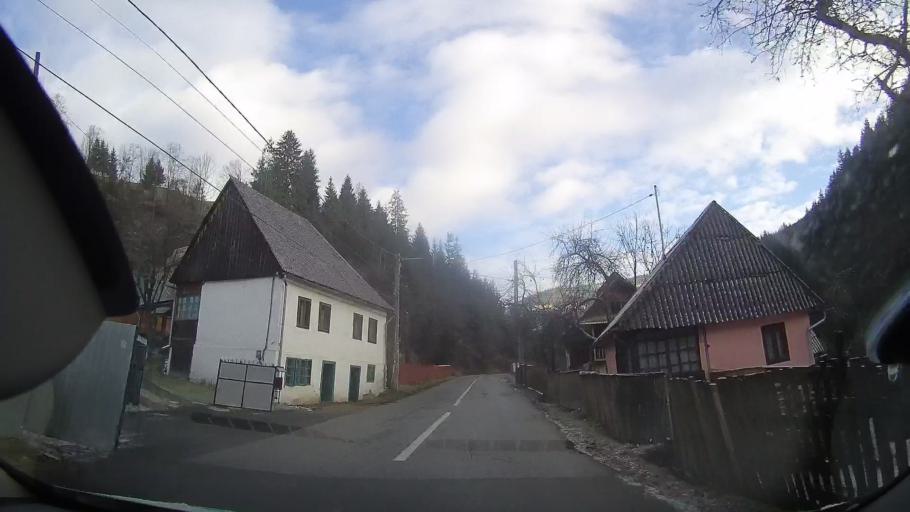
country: RO
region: Alba
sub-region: Comuna Albac
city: Albac
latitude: 46.4499
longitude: 22.9679
